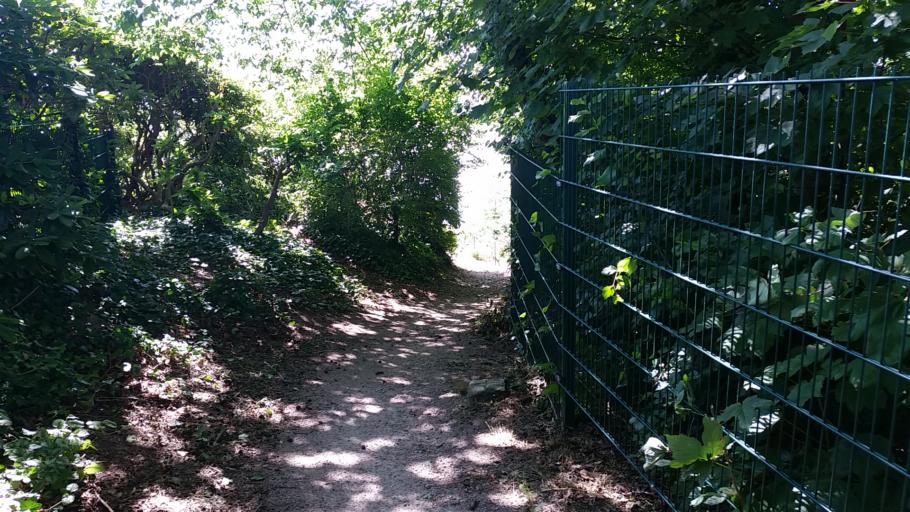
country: DE
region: Schleswig-Holstein
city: Halstenbek
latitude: 53.5594
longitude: 9.7962
